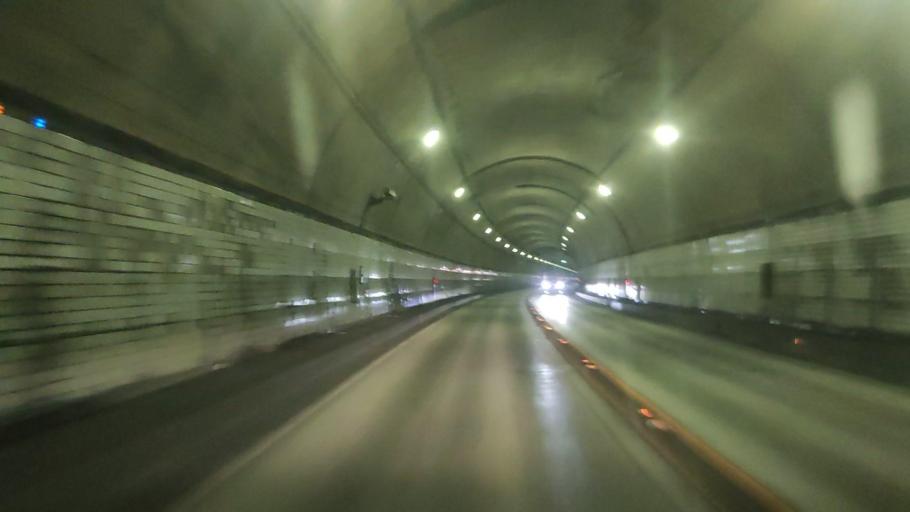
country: JP
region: Fukuoka
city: Maebaru-chuo
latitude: 33.4781
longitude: 130.2881
